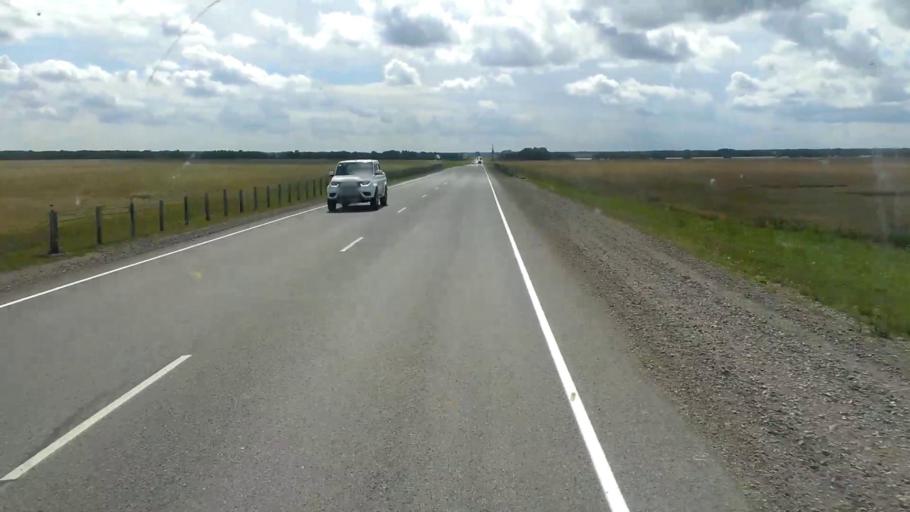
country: RU
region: Altai Krai
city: Troitskoye
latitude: 52.9034
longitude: 84.8310
